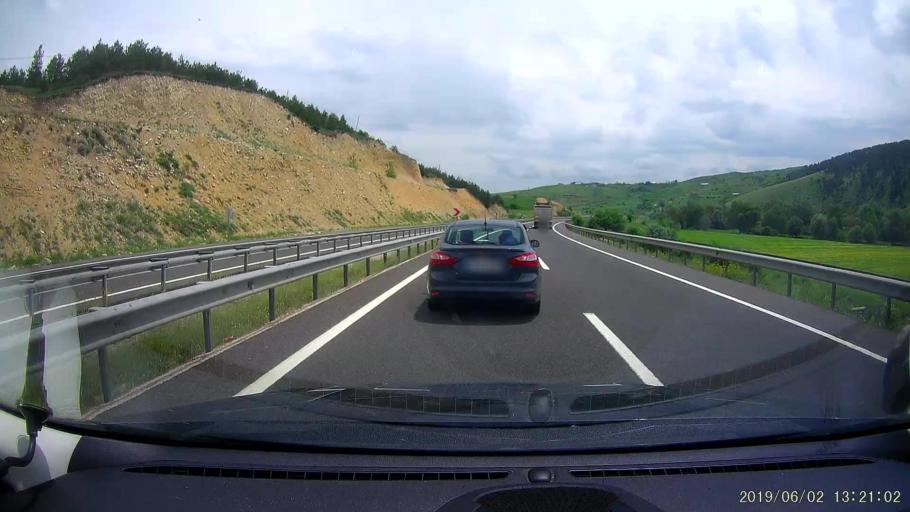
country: TR
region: Cankiri
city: Cerkes
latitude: 40.8389
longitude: 32.7723
